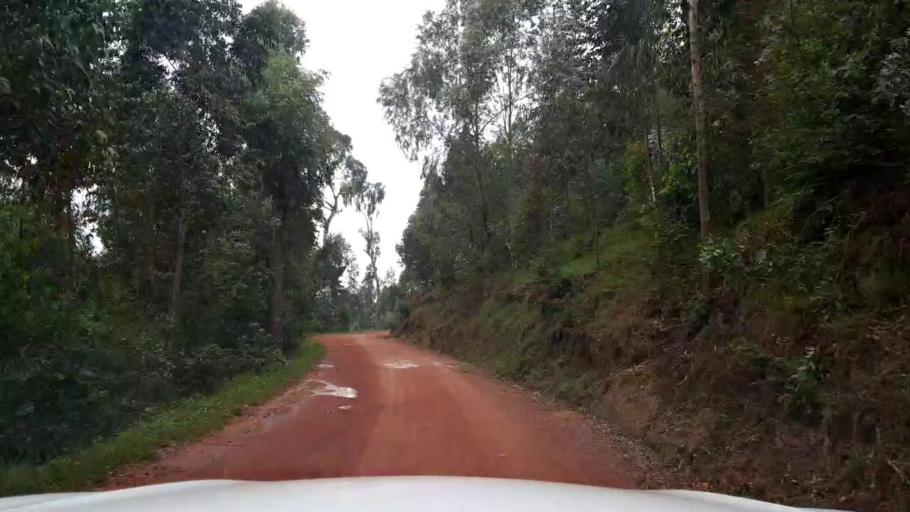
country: RW
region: Northern Province
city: Byumba
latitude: -1.5224
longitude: 29.9518
